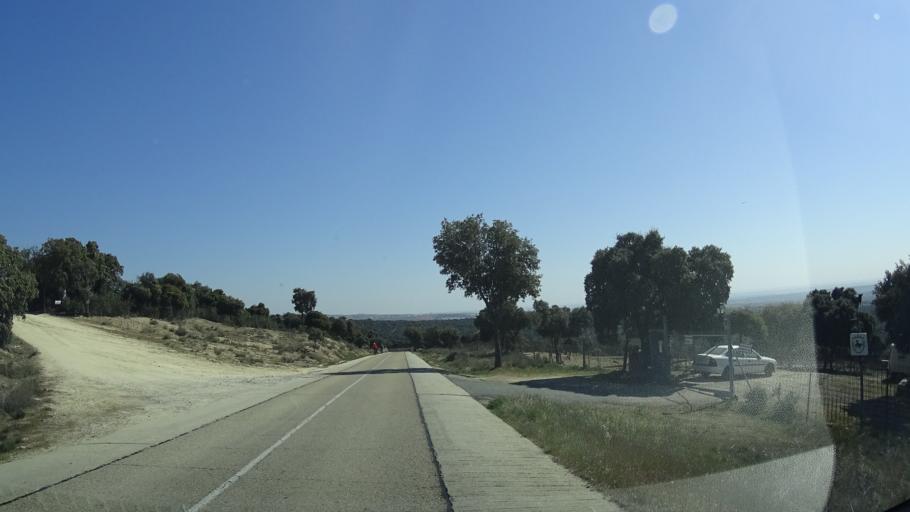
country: ES
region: Madrid
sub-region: Provincia de Madrid
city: Hoyo de Manzanares
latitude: 40.6369
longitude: -3.8539
